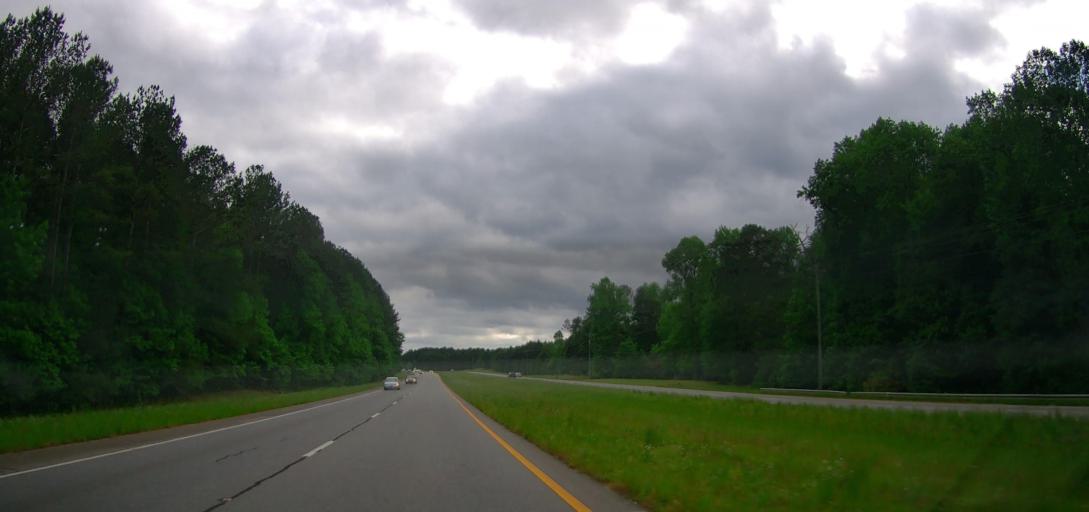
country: US
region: Georgia
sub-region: Walton County
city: Monroe
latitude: 33.8418
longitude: -83.6364
